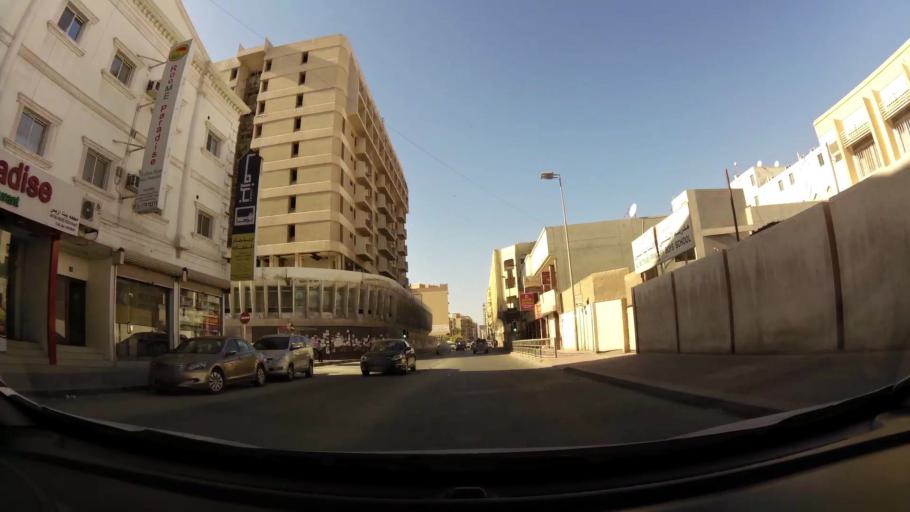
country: BH
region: Manama
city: Manama
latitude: 26.2252
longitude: 50.5833
